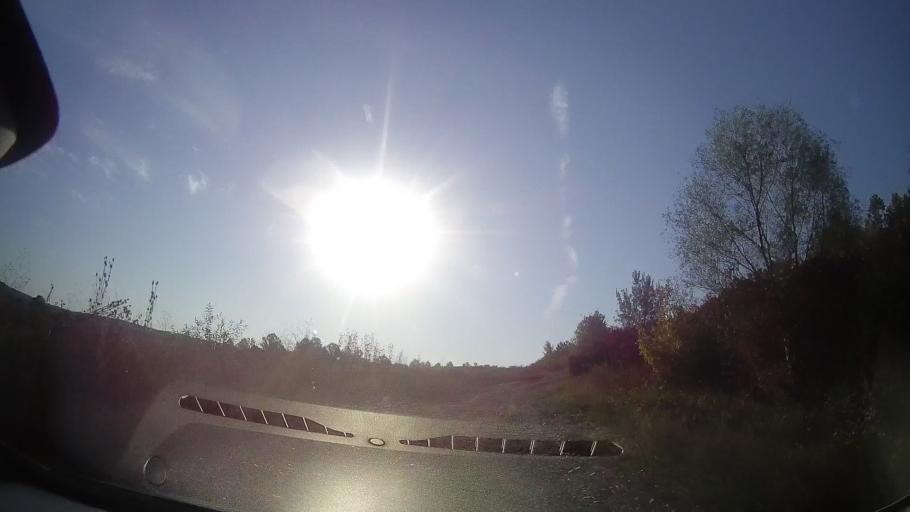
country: RO
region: Timis
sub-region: Comuna Bogda
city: Bogda
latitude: 45.9485
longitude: 21.6192
